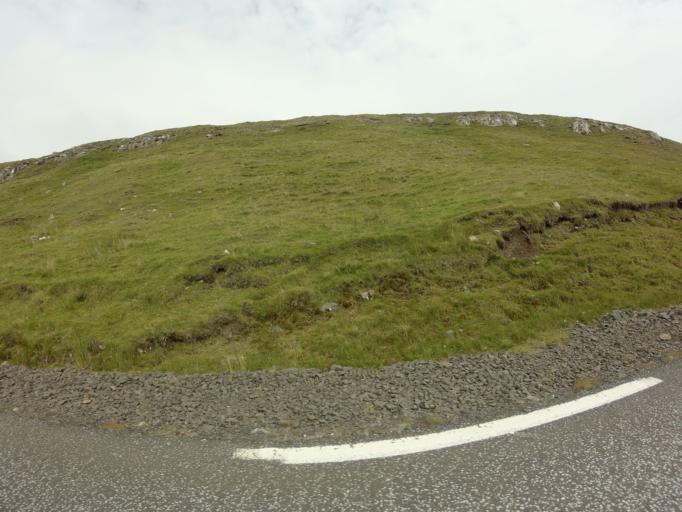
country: FO
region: Sandoy
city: Sandur
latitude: 61.8252
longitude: -6.7407
